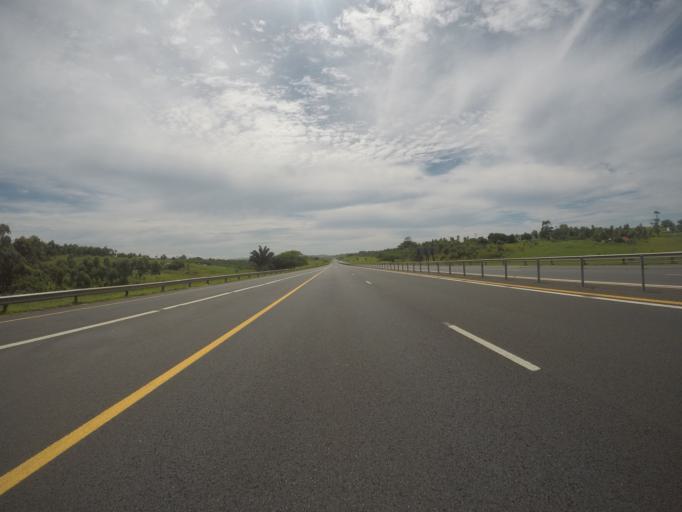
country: ZA
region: KwaZulu-Natal
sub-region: iLembe District Municipality
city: Mandeni
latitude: -29.1828
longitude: 31.4875
